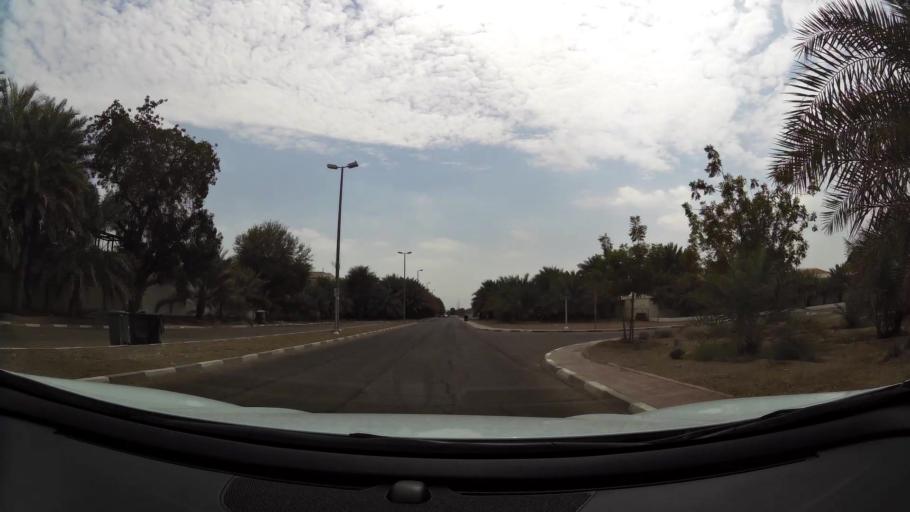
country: AE
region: Abu Dhabi
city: Al Ain
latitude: 24.2012
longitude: 55.7986
